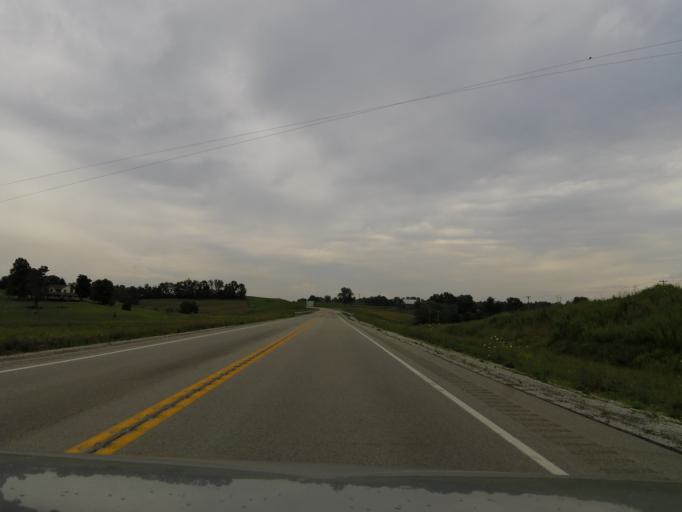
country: US
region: Ohio
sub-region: Brown County
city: Aberdeen
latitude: 38.6268
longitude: -83.8372
